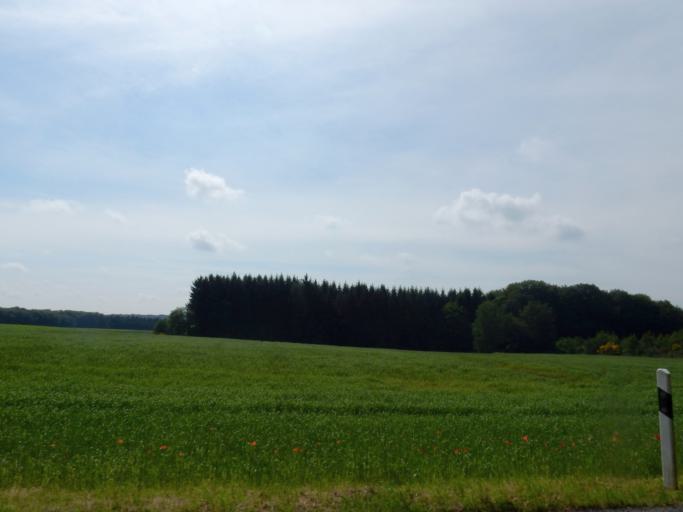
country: LU
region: Luxembourg
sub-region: Canton de Capellen
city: Septfontaines
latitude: 49.7106
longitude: 5.9530
